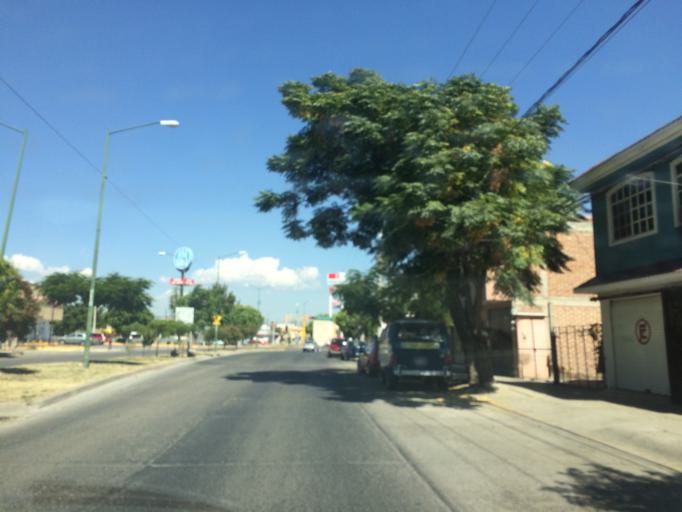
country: MX
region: Guanajuato
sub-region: Leon
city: San Jose de Duran (Los Troncoso)
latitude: 21.0793
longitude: -101.6518
